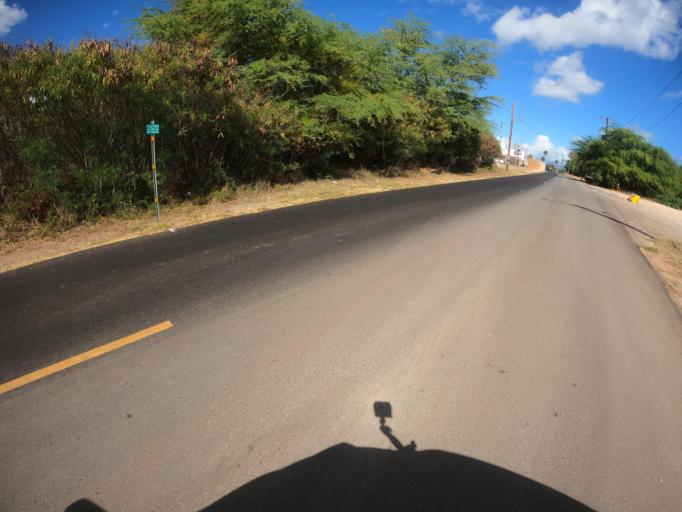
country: US
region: Hawaii
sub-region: Honolulu County
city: Makakilo City
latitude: 21.2994
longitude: -158.0728
